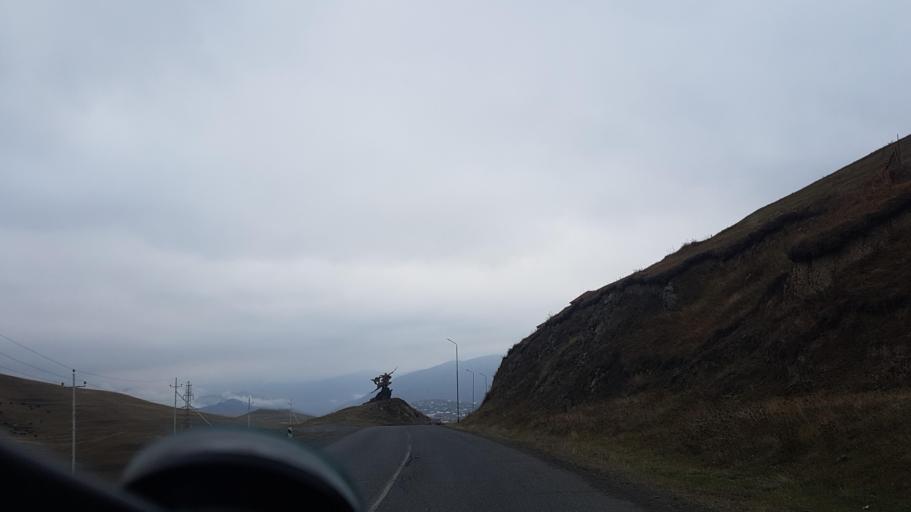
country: AZ
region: Gadabay Rayon
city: Ariqdam
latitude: 40.6146
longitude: 45.8110
